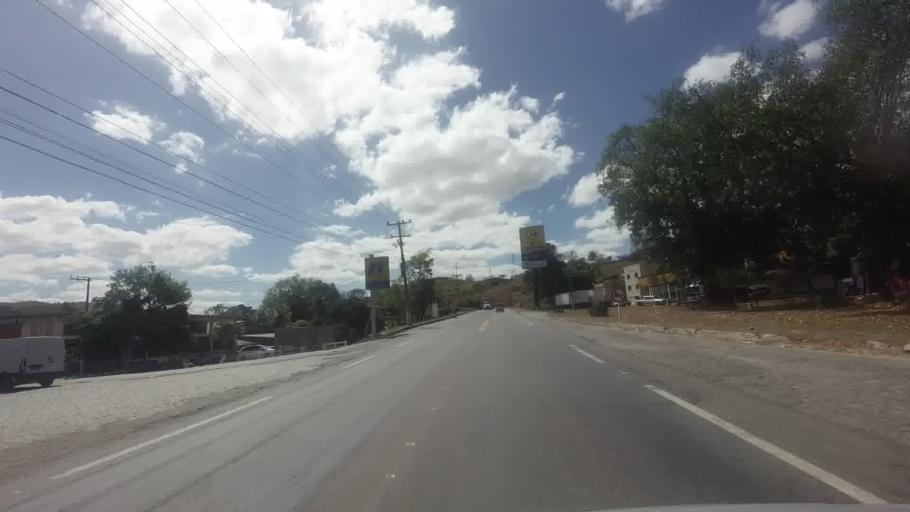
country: BR
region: Minas Gerais
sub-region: Alem Paraiba
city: Alem Paraiba
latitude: -21.8775
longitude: -42.6714
